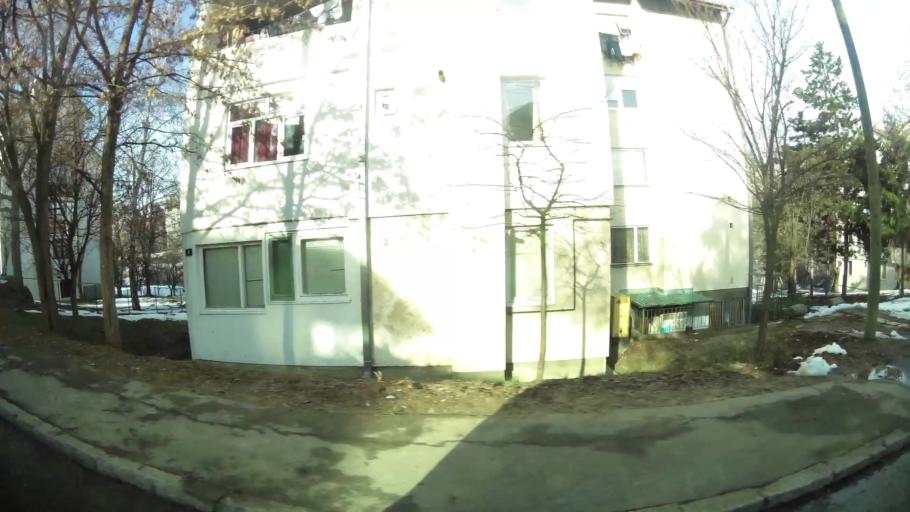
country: RS
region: Central Serbia
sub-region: Belgrade
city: Rakovica
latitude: 44.7216
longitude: 20.4258
